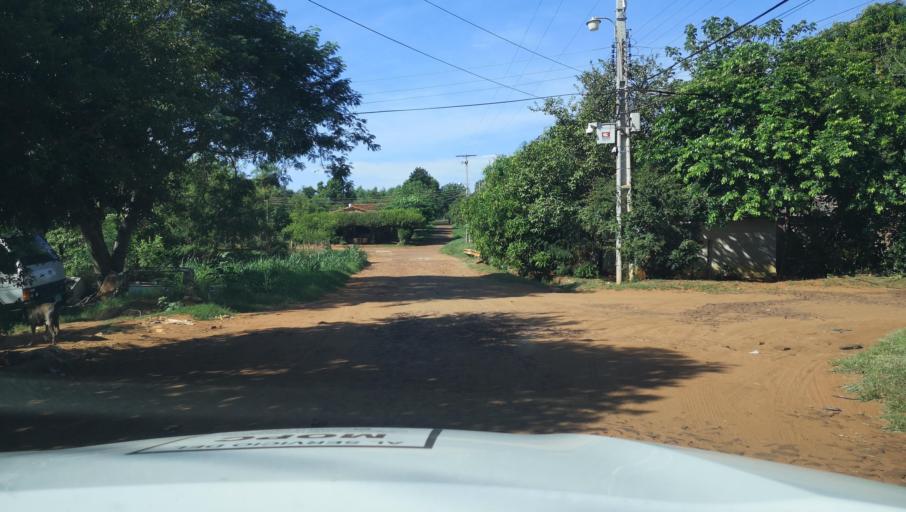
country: PY
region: Misiones
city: Santa Maria
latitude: -26.8944
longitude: -57.0181
